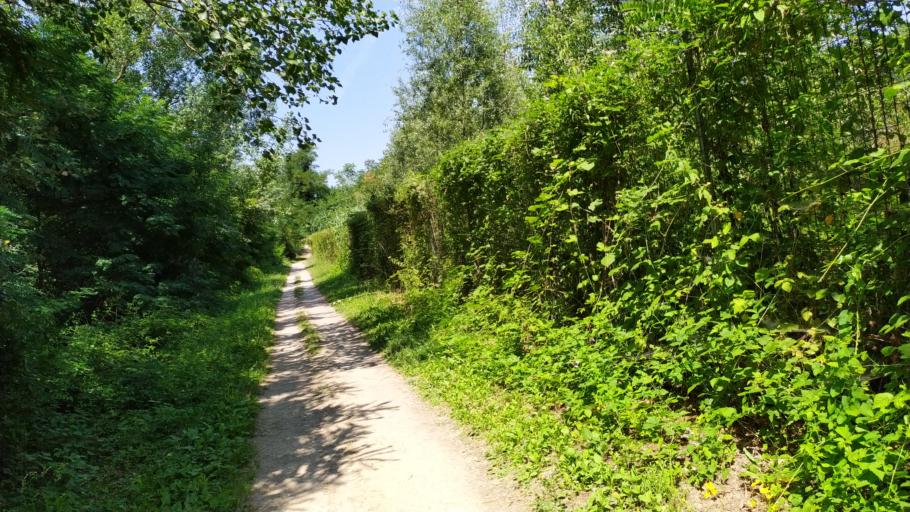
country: IT
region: Emilia-Romagna
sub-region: Forli-Cesena
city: Castrocaro Terme e Terra del Sole
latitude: 44.2038
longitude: 12.0051
